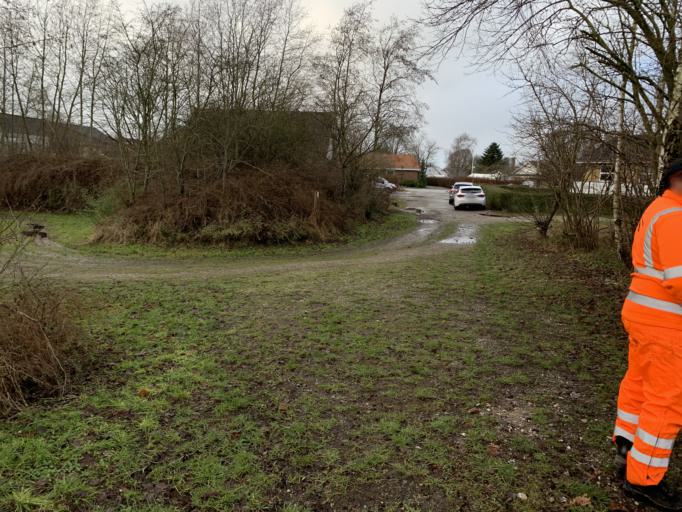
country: DK
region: North Denmark
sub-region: Mariagerfjord Kommune
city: Arden
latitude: 56.7085
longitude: 9.8375
